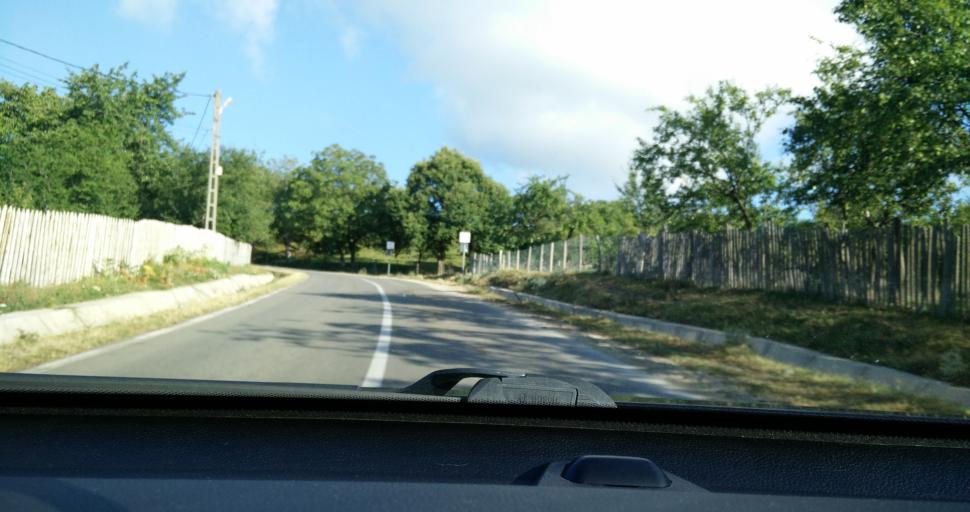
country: RO
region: Gorj
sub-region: Comuna Baia de Fier
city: Baia de Fier
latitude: 45.1770
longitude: 23.7811
